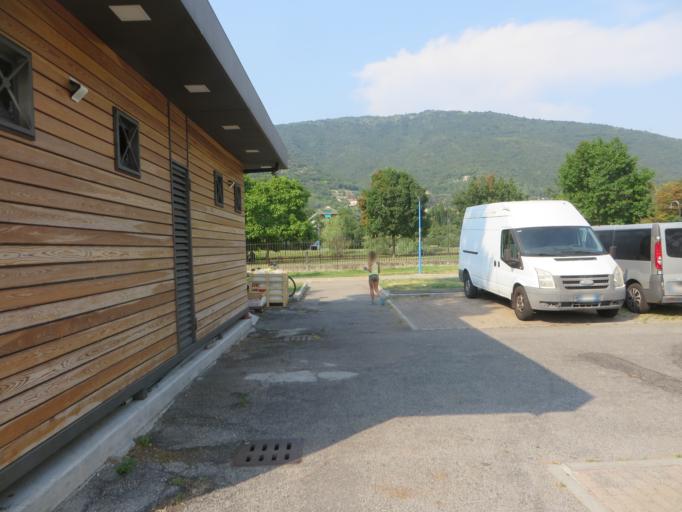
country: IT
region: Lombardy
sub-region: Provincia di Brescia
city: Brescia
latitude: 45.5269
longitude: 10.2491
